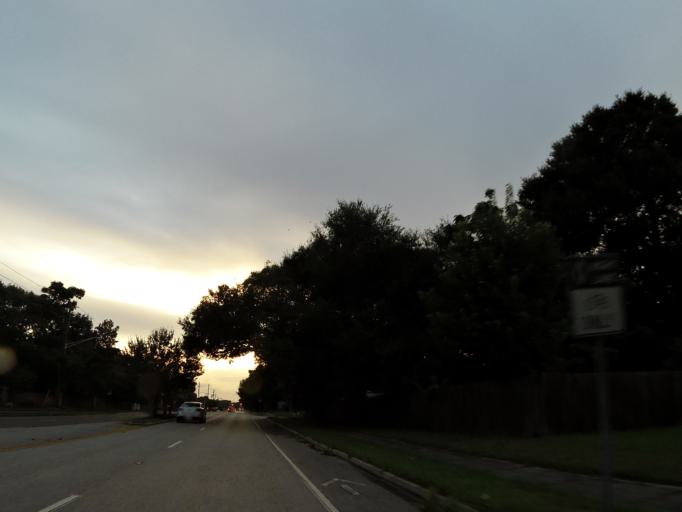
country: US
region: Florida
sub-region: Duval County
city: Jacksonville
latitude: 30.3666
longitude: -81.5844
